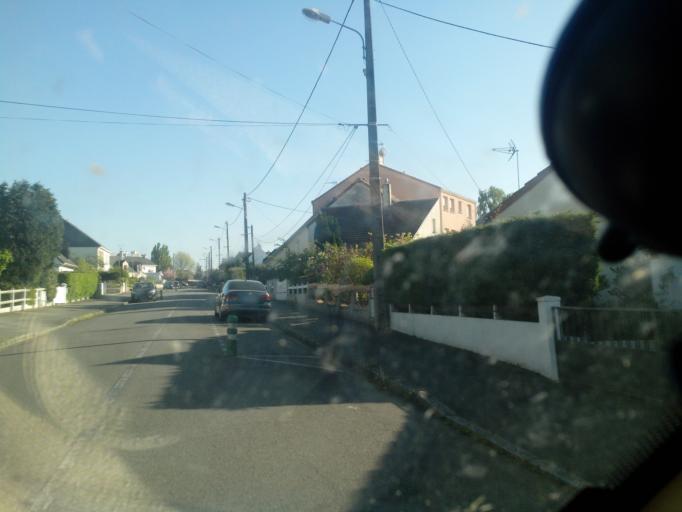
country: FR
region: Pays de la Loire
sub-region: Departement de la Loire-Atlantique
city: Orvault
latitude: 47.2513
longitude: -1.6007
